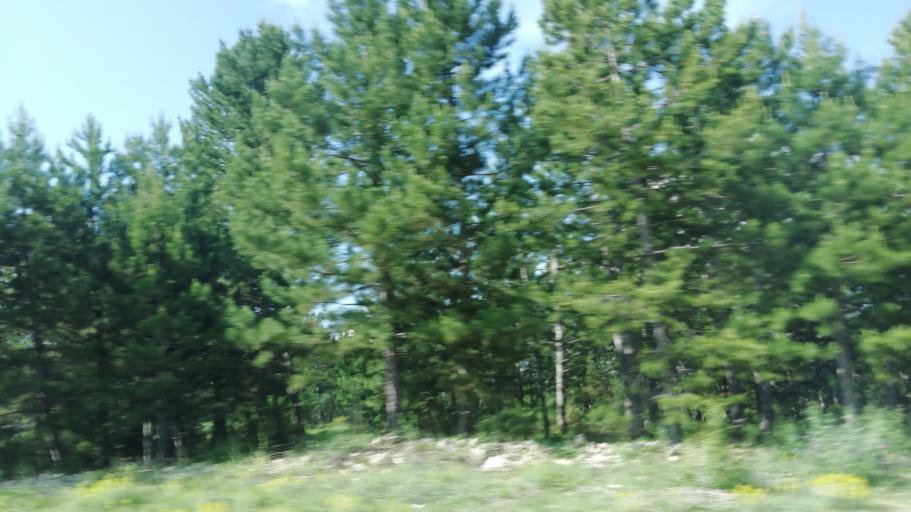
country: TR
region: Karabuk
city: Karabuk
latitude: 41.1257
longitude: 32.5950
